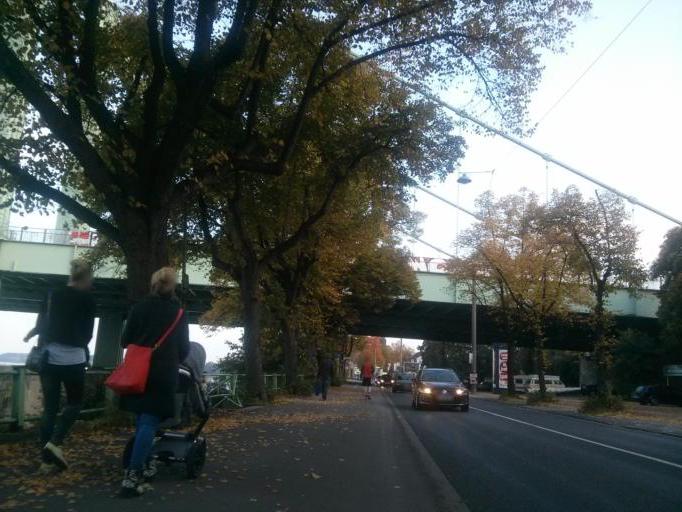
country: DE
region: North Rhine-Westphalia
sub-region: Regierungsbezirk Koln
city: Poll
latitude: 50.8986
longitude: 6.9876
